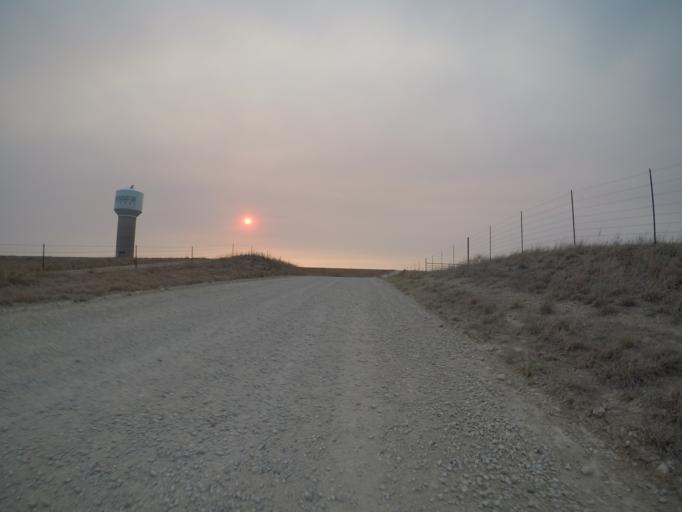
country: US
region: Kansas
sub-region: Riley County
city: Manhattan
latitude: 39.2306
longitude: -96.6449
